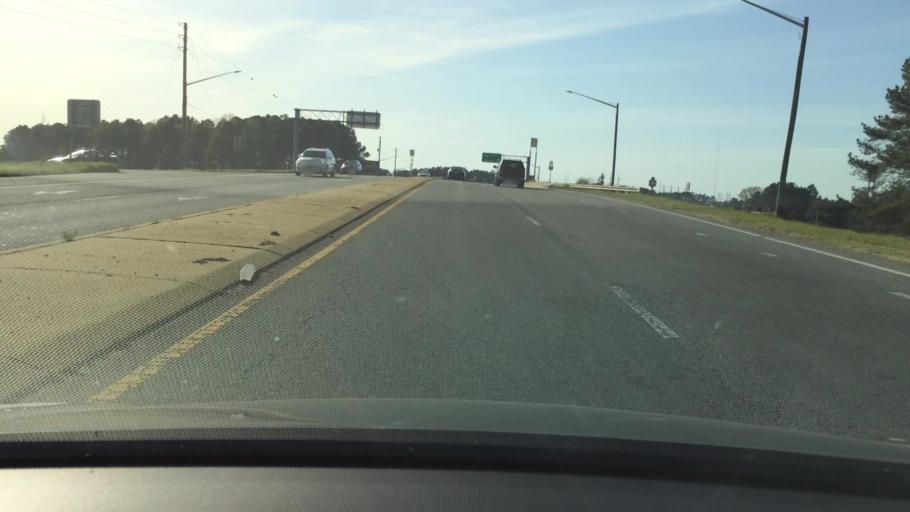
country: US
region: North Carolina
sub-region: Johnston County
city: Selma
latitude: 35.5189
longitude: -78.2882
